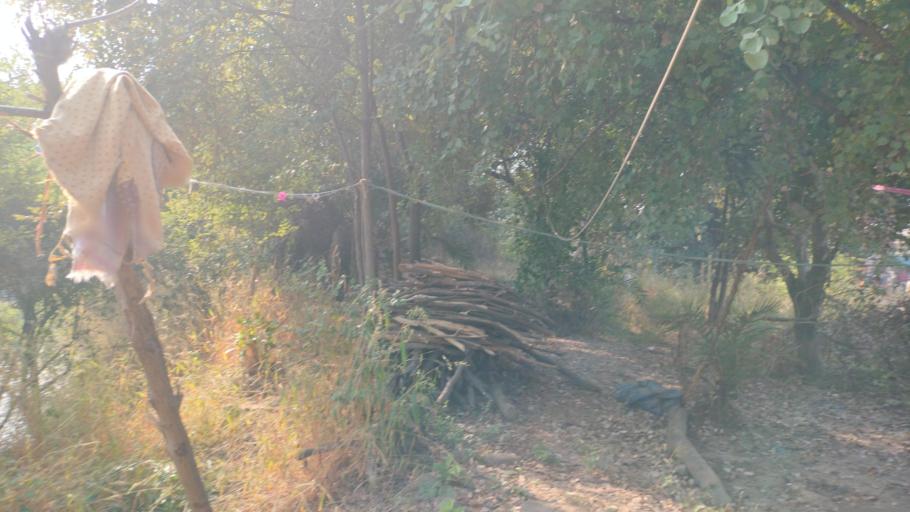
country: IN
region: Maharashtra
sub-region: Thane
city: Virar
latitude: 19.3937
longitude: 72.8581
